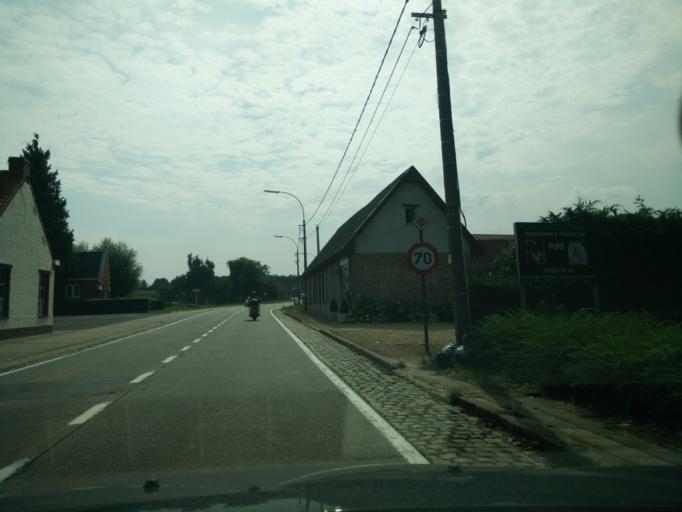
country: BE
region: Flanders
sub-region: Provincie Oost-Vlaanderen
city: Merelbeke
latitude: 50.9474
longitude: 3.7347
